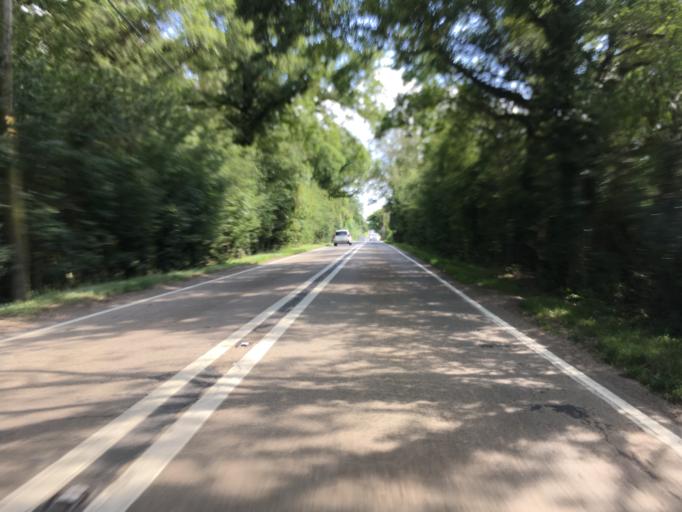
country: GB
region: England
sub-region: Kent
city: Headcorn
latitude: 51.1553
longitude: 0.6353
